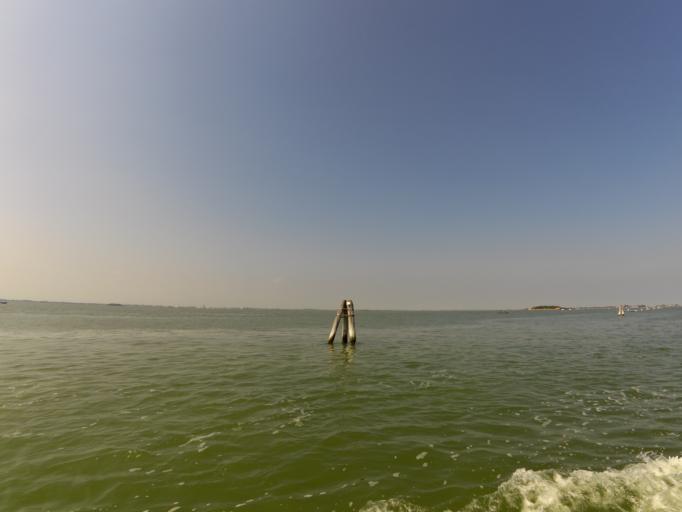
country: IT
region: Veneto
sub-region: Provincia di Venezia
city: Murano
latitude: 45.4602
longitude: 12.3696
